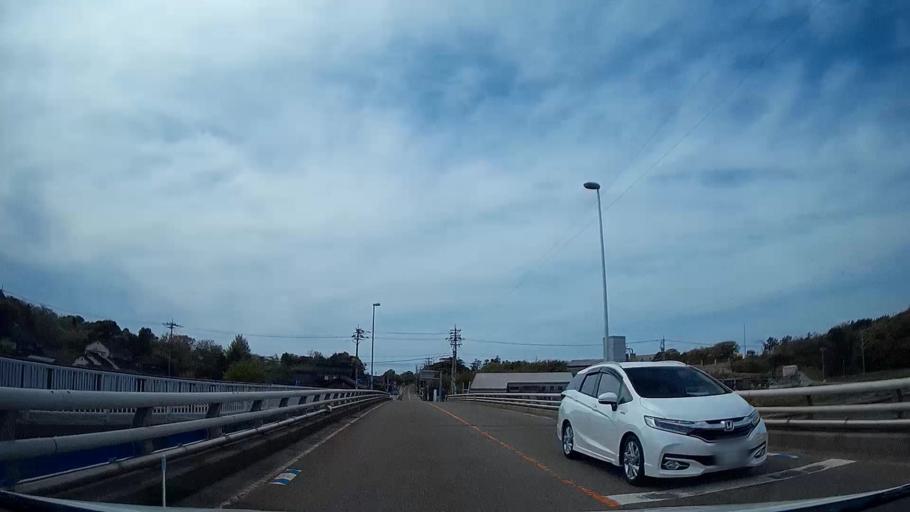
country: JP
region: Ishikawa
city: Hakui
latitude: 37.0067
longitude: 136.7691
